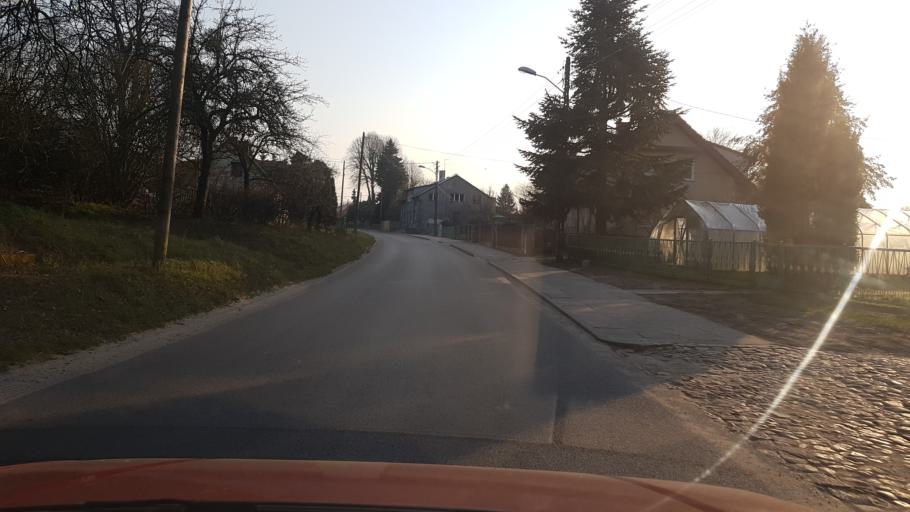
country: PL
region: West Pomeranian Voivodeship
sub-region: Powiat gryfinski
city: Stare Czarnowo
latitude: 53.3426
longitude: 14.7520
